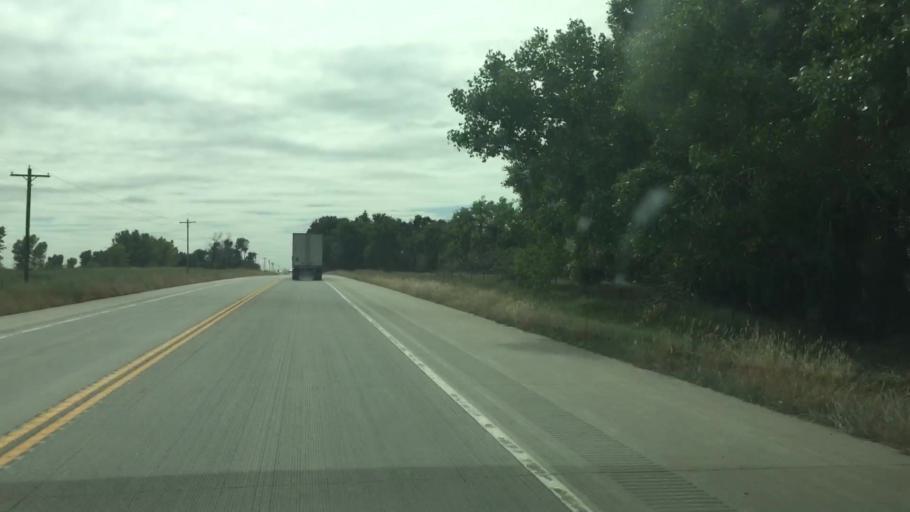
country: US
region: Colorado
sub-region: Prowers County
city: Lamar
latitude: 38.2080
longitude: -102.7242
